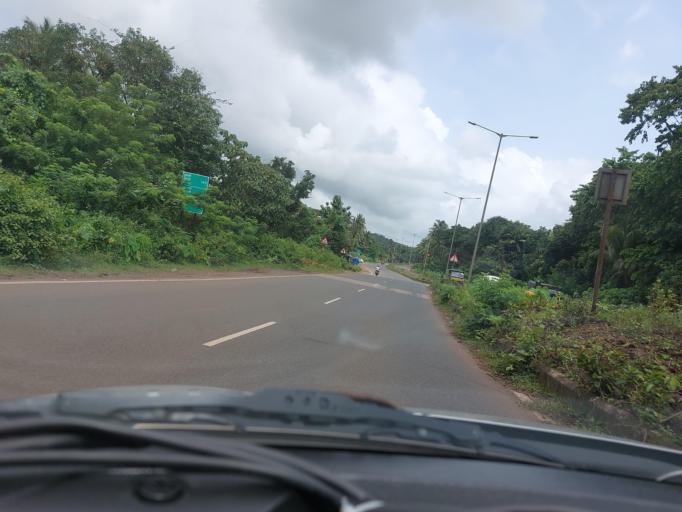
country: IN
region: Goa
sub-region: North Goa
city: Queula
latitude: 15.3875
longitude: 73.9988
